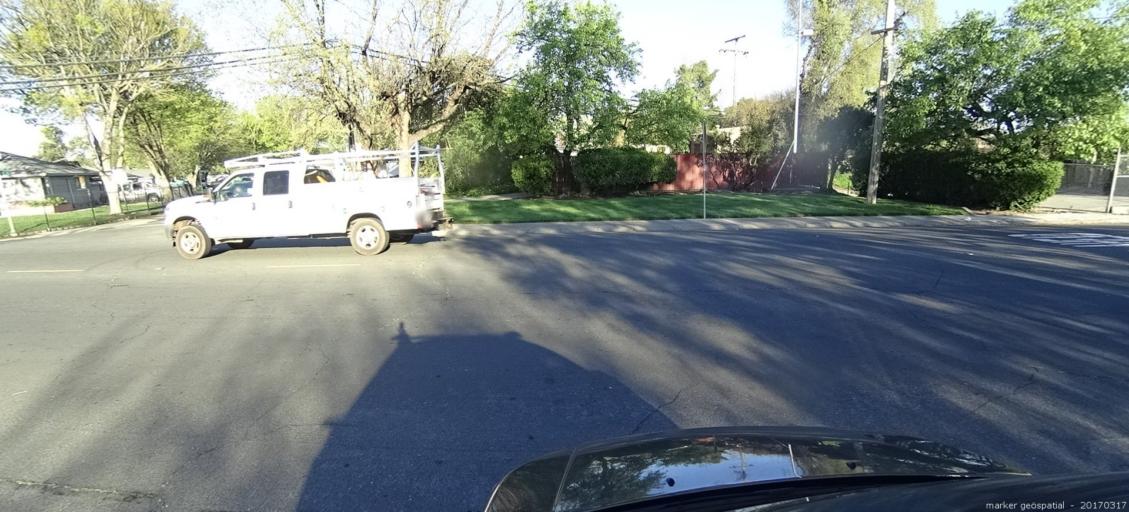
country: US
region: California
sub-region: Sacramento County
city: Parkway
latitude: 38.4941
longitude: -121.4916
